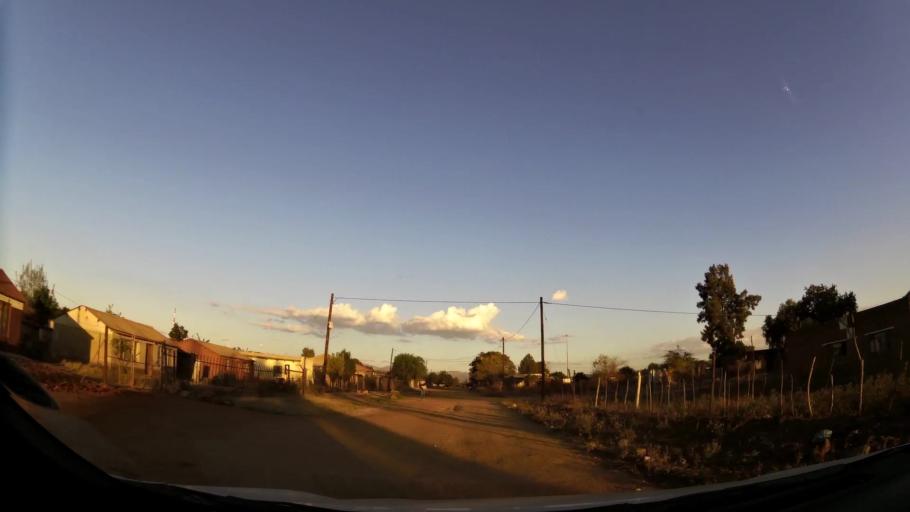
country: ZA
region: Limpopo
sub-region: Waterberg District Municipality
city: Mokopane
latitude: -24.1463
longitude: 28.9758
